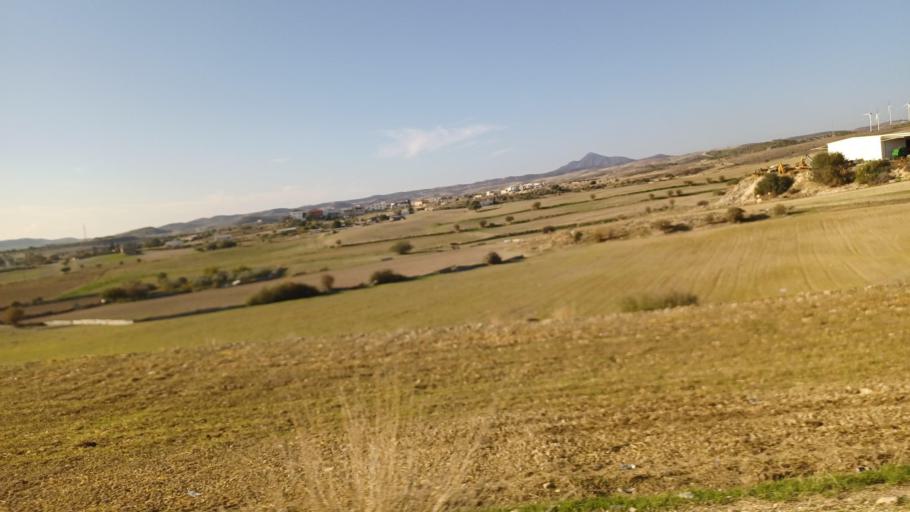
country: CY
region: Larnaka
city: Aradippou
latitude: 34.9354
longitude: 33.5299
